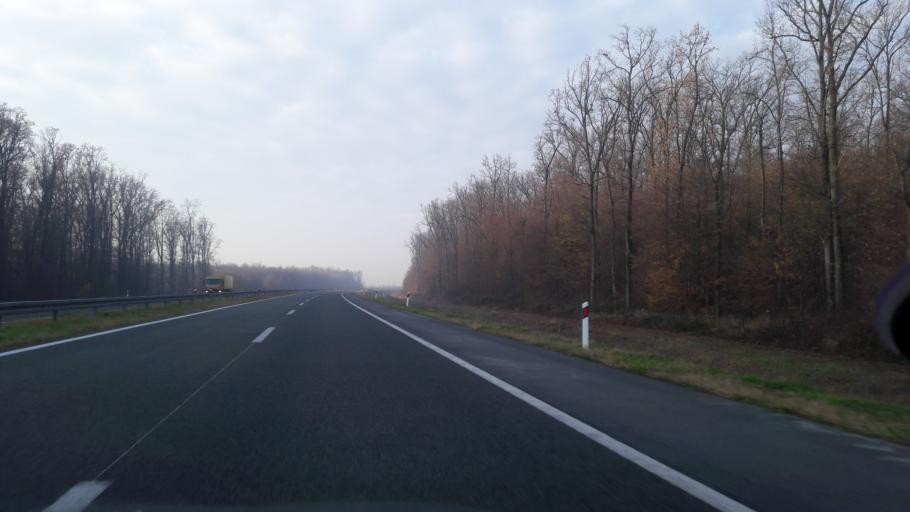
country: HR
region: Osjecko-Baranjska
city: Vuka
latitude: 45.4191
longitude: 18.4496
